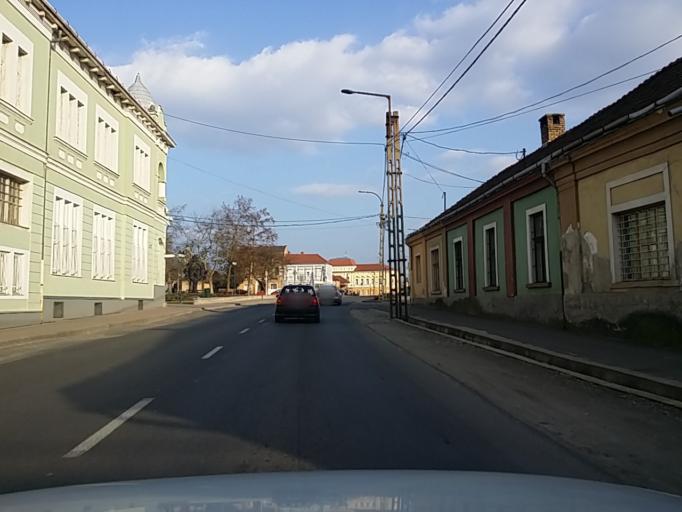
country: HU
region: Borsod-Abauj-Zemplen
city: Putnok
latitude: 48.2953
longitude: 20.4315
